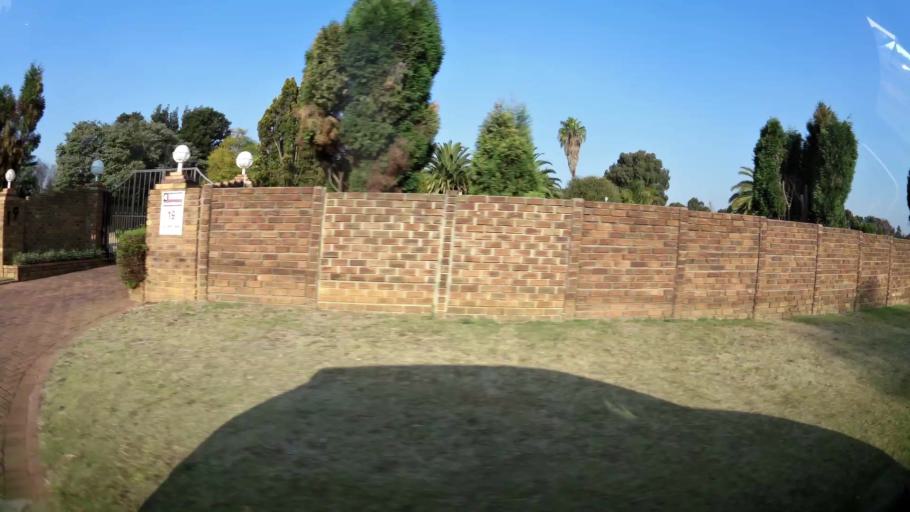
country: ZA
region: Gauteng
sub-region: Ekurhuleni Metropolitan Municipality
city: Benoni
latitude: -26.1388
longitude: 28.3611
